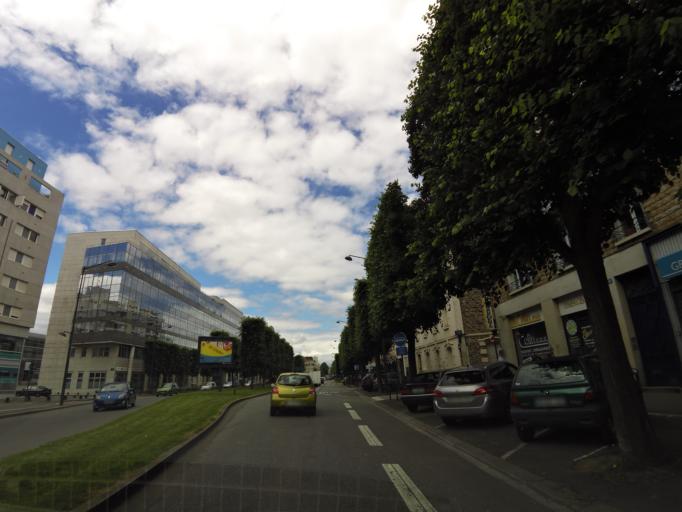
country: FR
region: Brittany
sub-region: Departement d'Ille-et-Vilaine
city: Rennes
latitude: 48.1036
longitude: -1.6844
